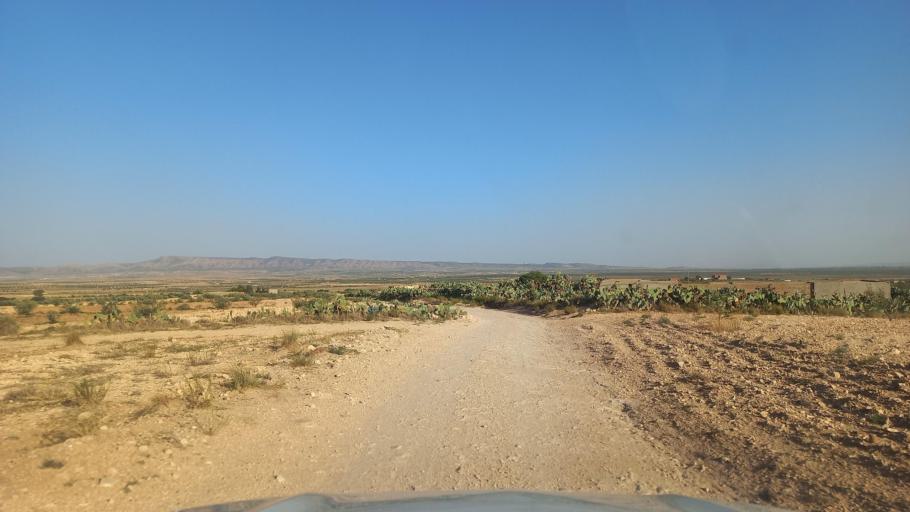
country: TN
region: Al Qasrayn
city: Sbiba
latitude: 35.3670
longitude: 9.0116
